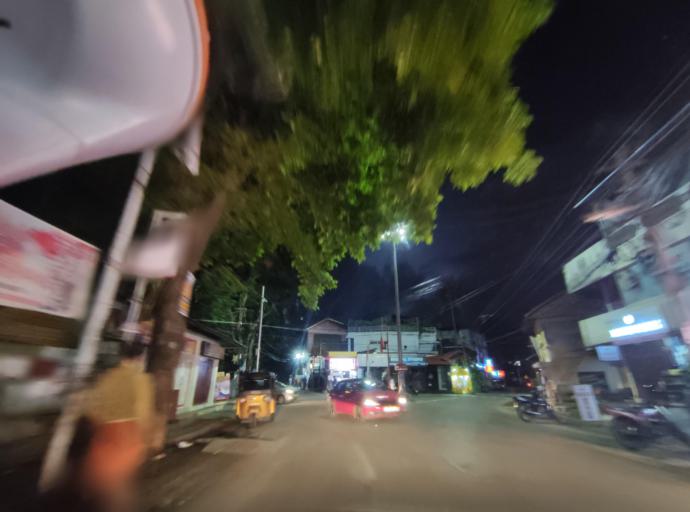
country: IN
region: Kerala
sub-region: Thiruvananthapuram
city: Nedumangad
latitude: 8.5639
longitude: 76.9530
